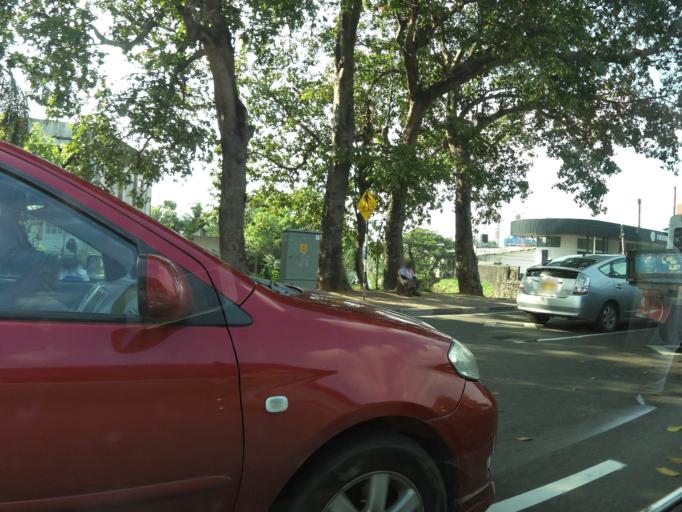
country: LK
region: Western
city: Kolonnawa
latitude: 6.9477
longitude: 79.8784
